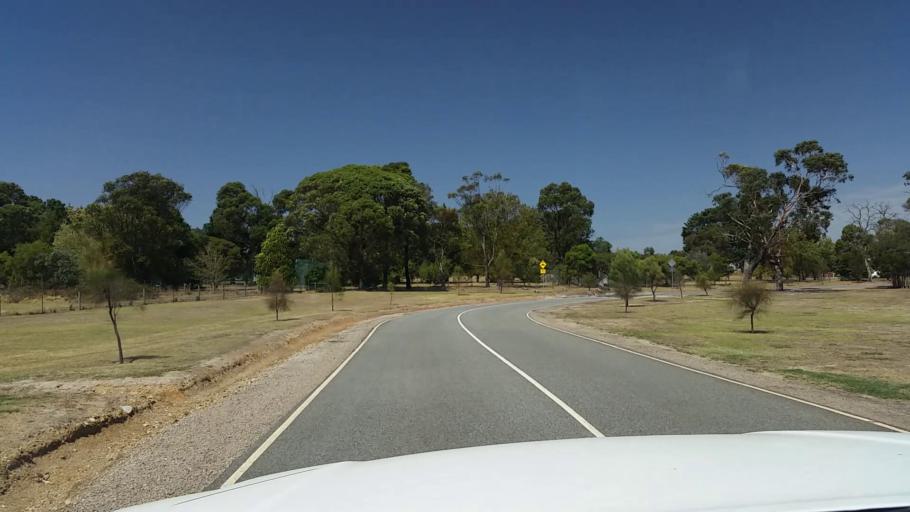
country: AU
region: Victoria
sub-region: Mornington Peninsula
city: Tyabb
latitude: -38.2656
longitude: 145.1916
